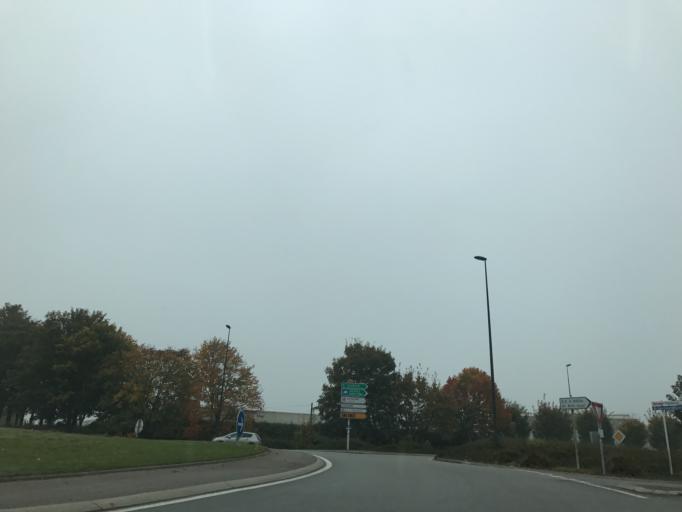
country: FR
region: Nord-Pas-de-Calais
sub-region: Departement du Pas-de-Calais
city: Bapaume
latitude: 50.1061
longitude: 2.8665
